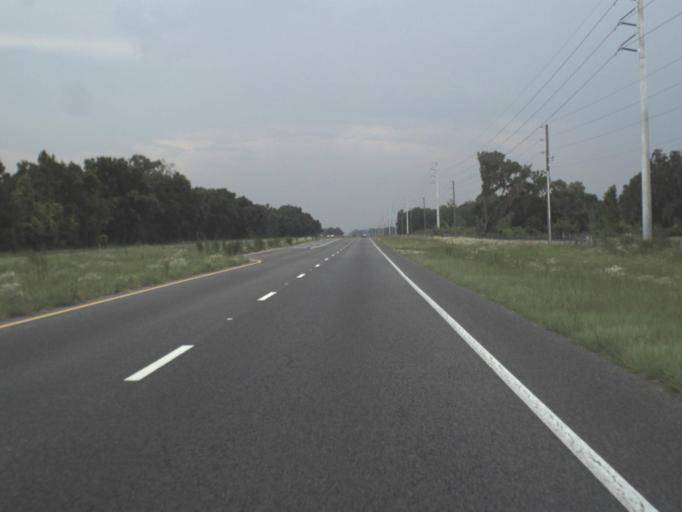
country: US
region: Florida
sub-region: Levy County
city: Chiefland
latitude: 29.4749
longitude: -82.7671
